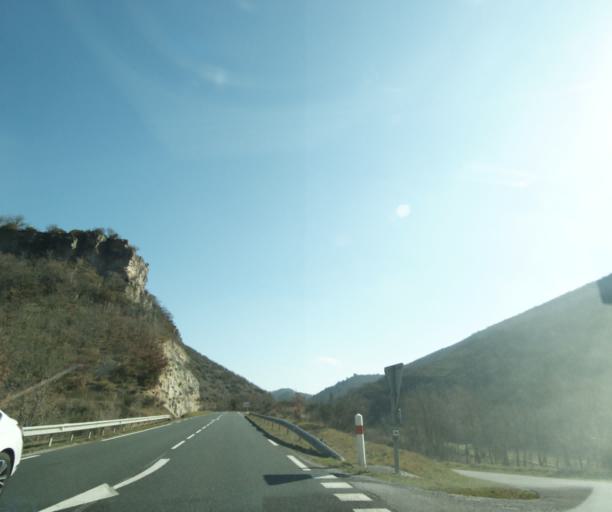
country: FR
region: Midi-Pyrenees
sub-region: Departement de l'Aveyron
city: Saint-Affrique
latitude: 43.9546
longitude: 2.9330
